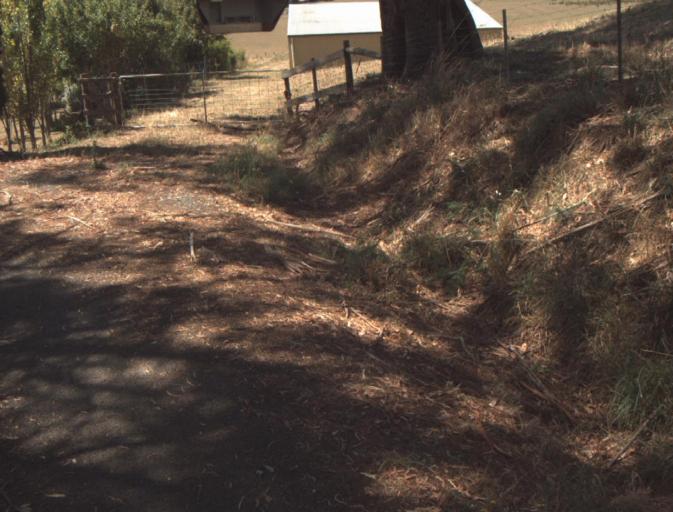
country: AU
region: Tasmania
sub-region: Launceston
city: Mayfield
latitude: -41.2588
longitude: 147.1442
